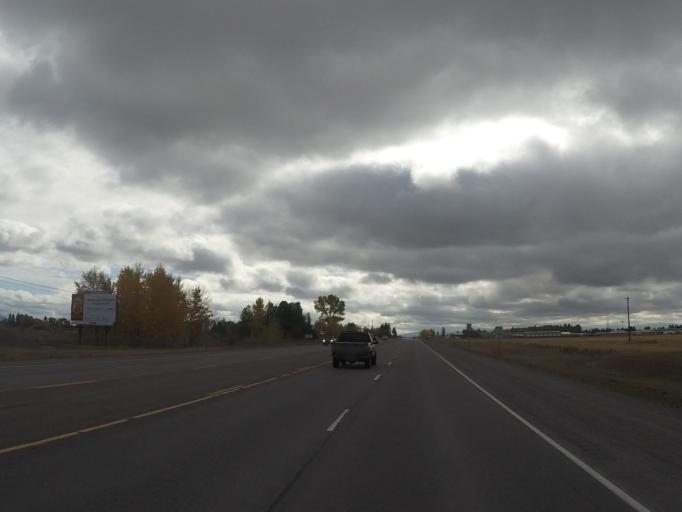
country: US
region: Montana
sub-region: Flathead County
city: Columbia Falls
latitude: 48.3683
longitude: -114.2410
